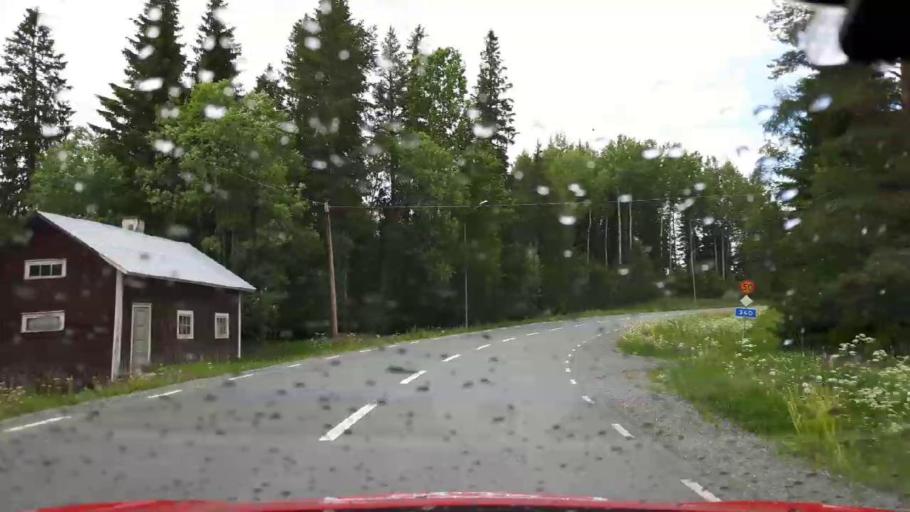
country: SE
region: Jaemtland
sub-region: Krokoms Kommun
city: Krokom
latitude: 63.5669
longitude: 14.2709
